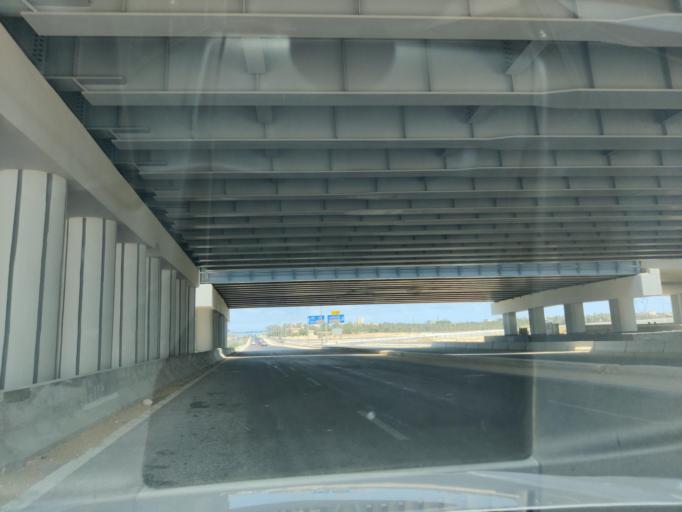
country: EG
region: Alexandria
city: Alexandria
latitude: 31.0034
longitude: 29.6414
